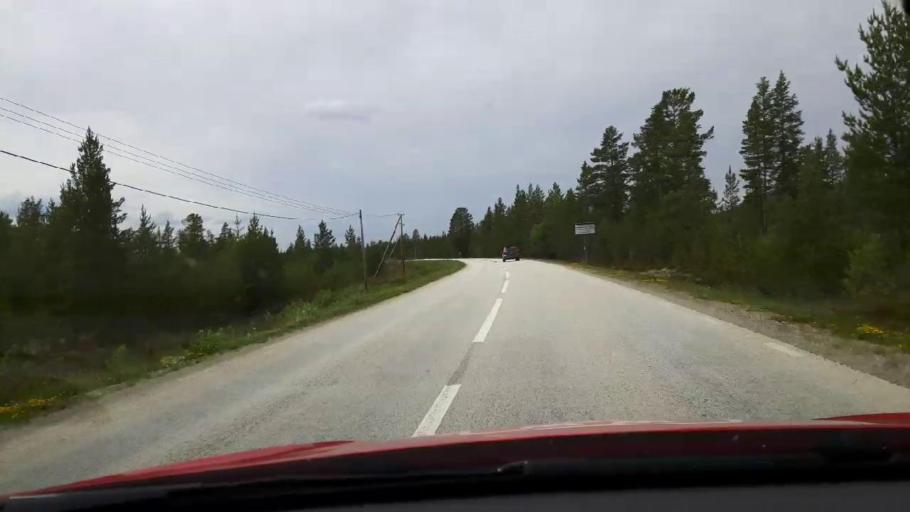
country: SE
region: Jaemtland
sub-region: Harjedalens Kommun
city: Sveg
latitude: 62.4056
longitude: 13.7295
